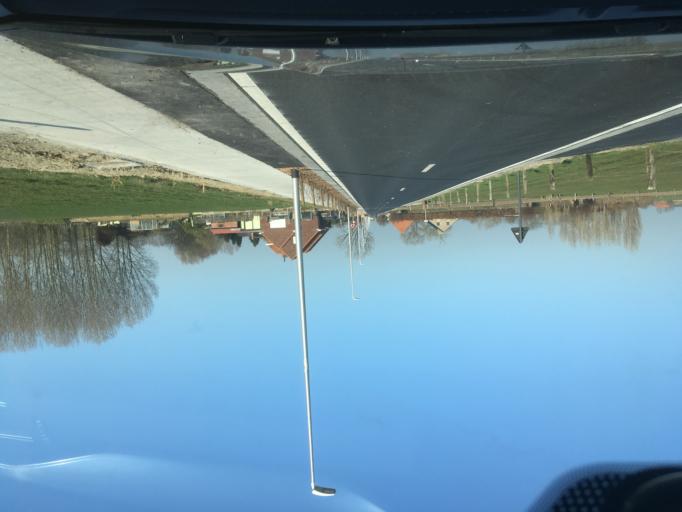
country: BE
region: Flanders
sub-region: Provincie West-Vlaanderen
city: Ledegem
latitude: 50.8698
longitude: 3.1544
